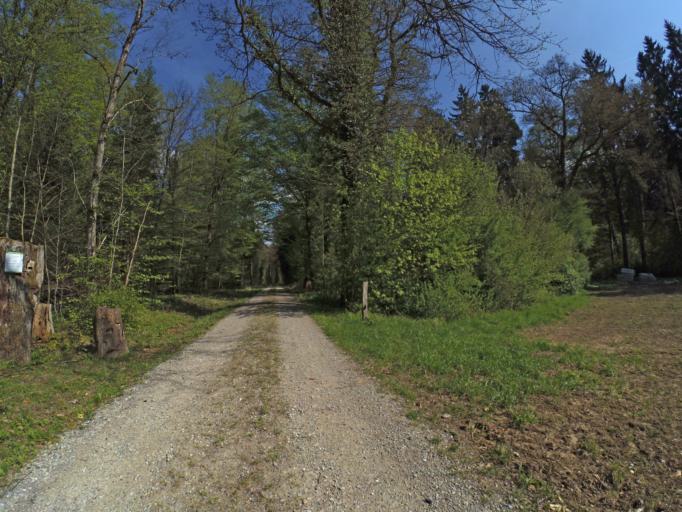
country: CH
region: Thurgau
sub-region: Frauenfeld District
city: Diessenhofen
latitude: 47.6485
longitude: 8.7442
